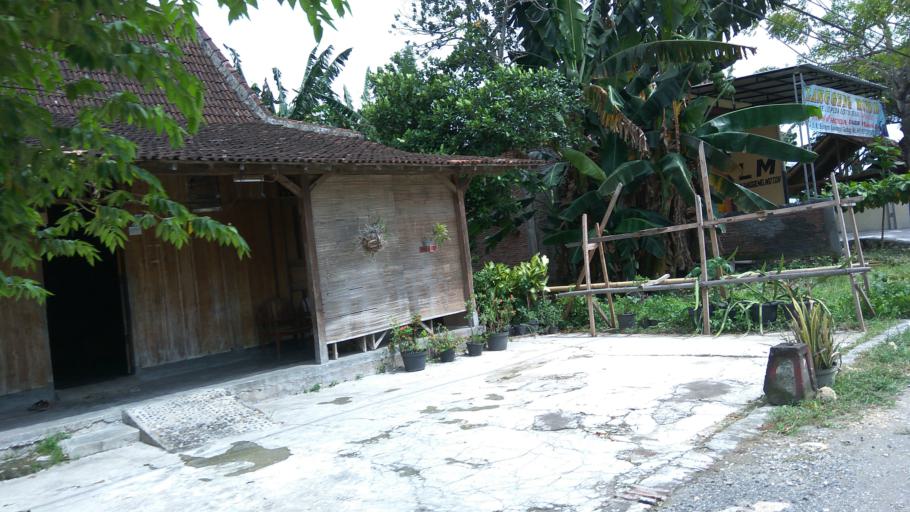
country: ID
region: Central Java
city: Mranggen
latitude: -7.0693
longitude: 110.6646
